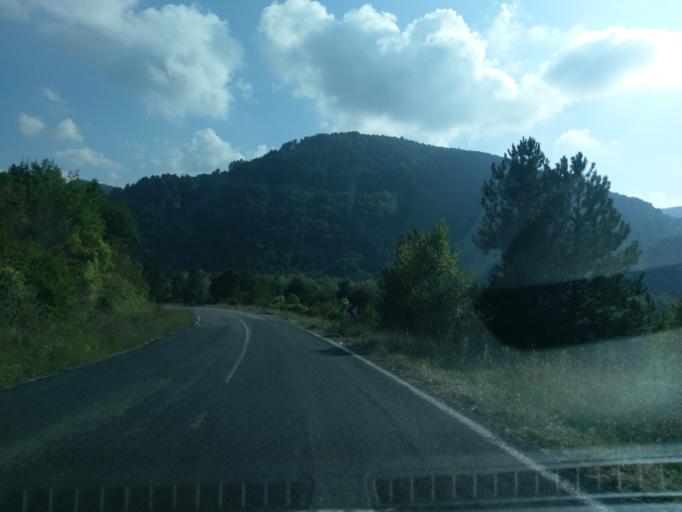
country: TR
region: Sinop
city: Yenikonak
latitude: 41.9412
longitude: 34.7227
